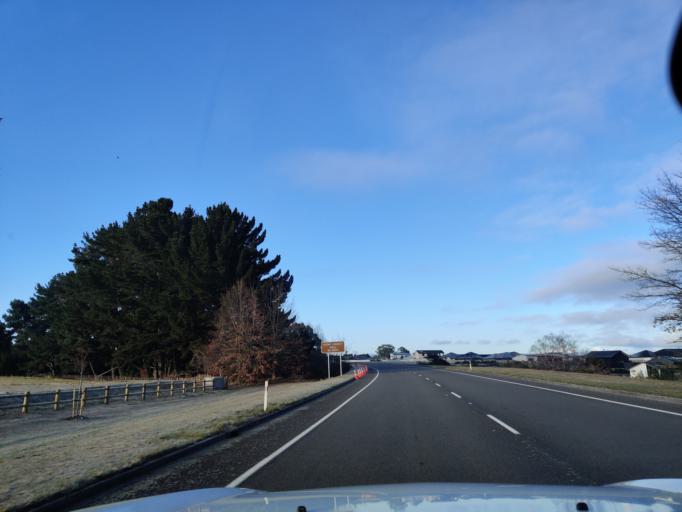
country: NZ
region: Waikato
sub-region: Taupo District
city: Taupo
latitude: -38.7329
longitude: 176.0725
